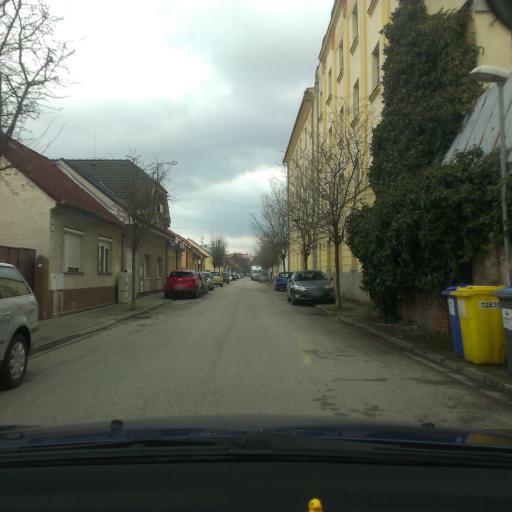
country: SK
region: Trnavsky
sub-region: Okres Trnava
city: Piestany
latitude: 48.5920
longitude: 17.8176
